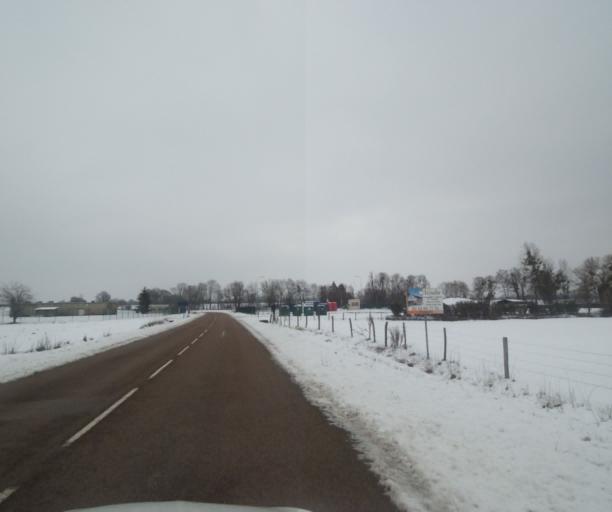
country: FR
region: Champagne-Ardenne
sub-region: Departement de la Haute-Marne
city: Villiers-en-Lieu
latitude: 48.5928
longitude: 4.8516
